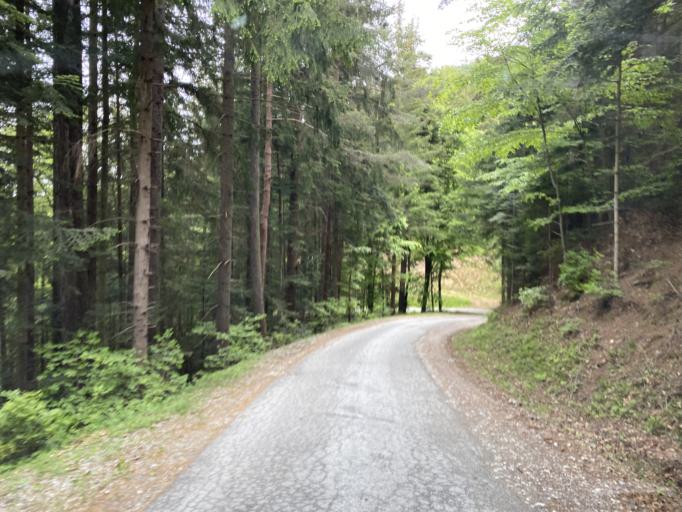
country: AT
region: Styria
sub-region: Politischer Bezirk Weiz
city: Koglhof
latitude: 47.3247
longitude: 15.7003
